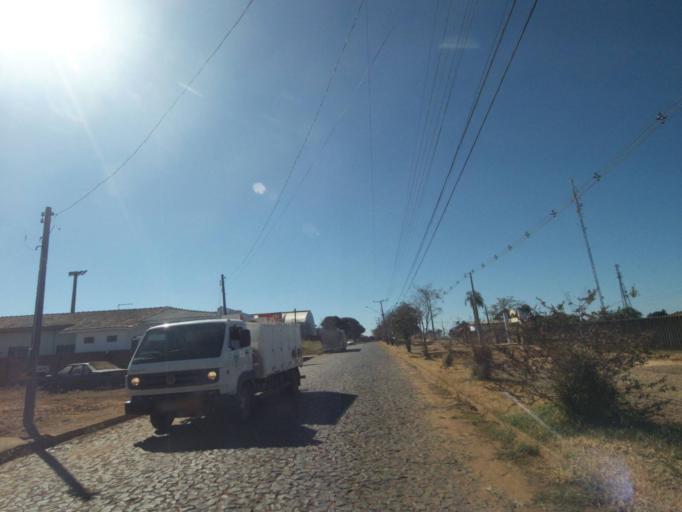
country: BR
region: Parana
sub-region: Reserva
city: Reserva
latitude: -24.6233
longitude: -50.6403
